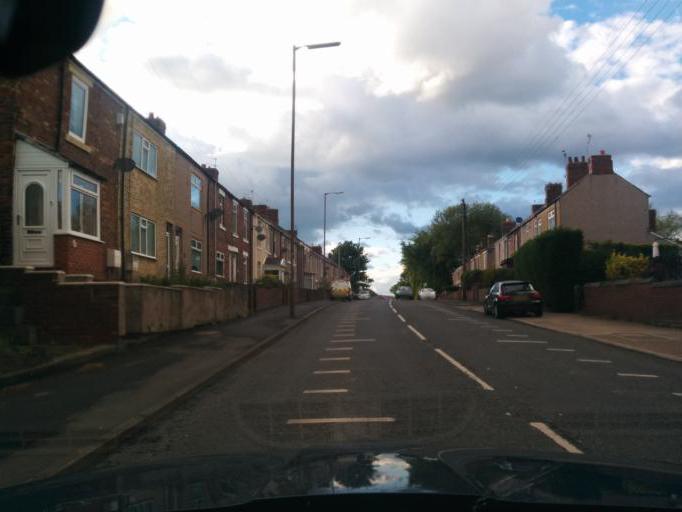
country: GB
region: England
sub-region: Northumberland
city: Choppington
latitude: 55.1478
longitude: -1.6014
